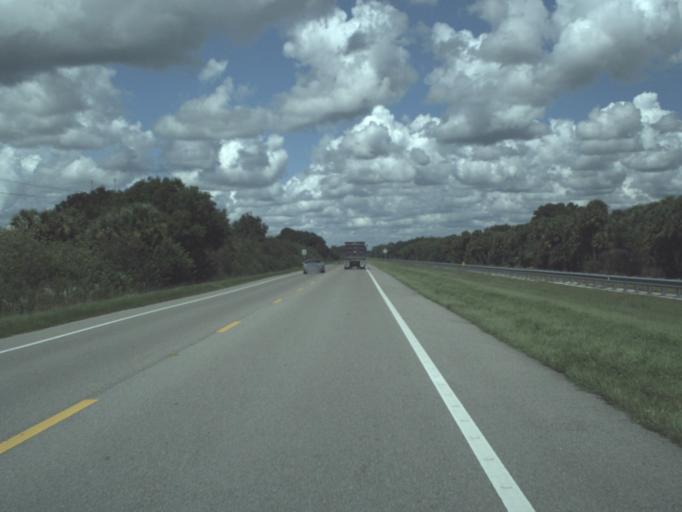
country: US
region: Florida
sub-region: Collier County
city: Immokalee
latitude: 26.3853
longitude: -81.3717
